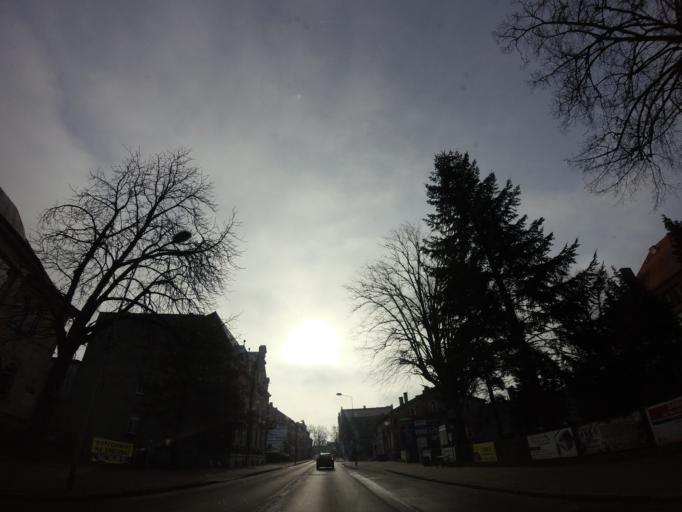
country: PL
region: West Pomeranian Voivodeship
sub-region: Powiat walecki
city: Walcz
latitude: 53.2742
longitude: 16.4657
